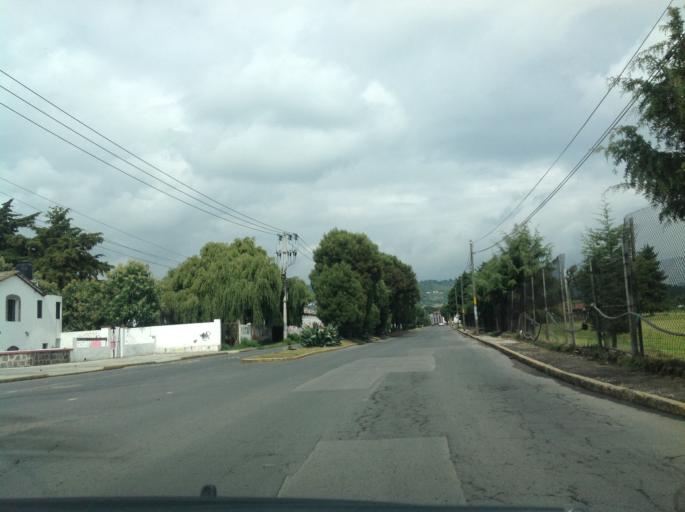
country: MX
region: Morelos
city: Tenango de Arista
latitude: 19.1053
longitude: -99.5800
